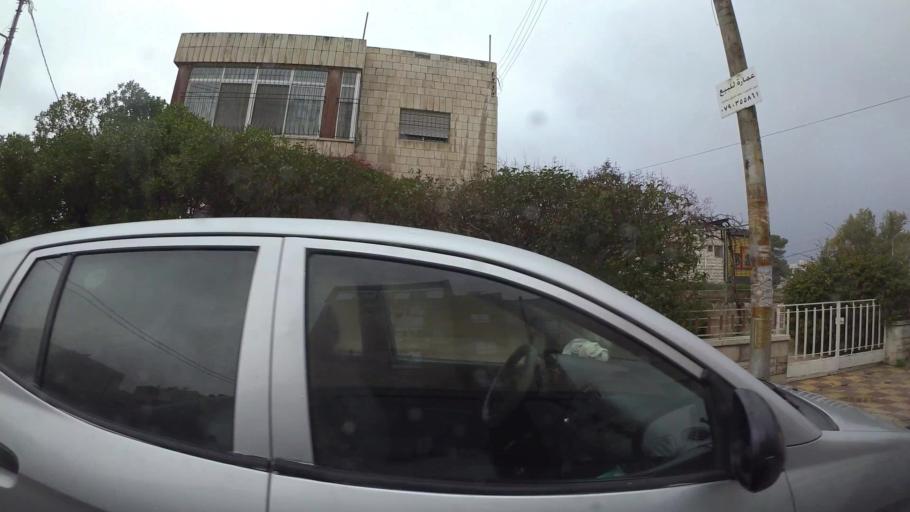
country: JO
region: Amman
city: Amman
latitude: 31.9656
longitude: 35.9169
